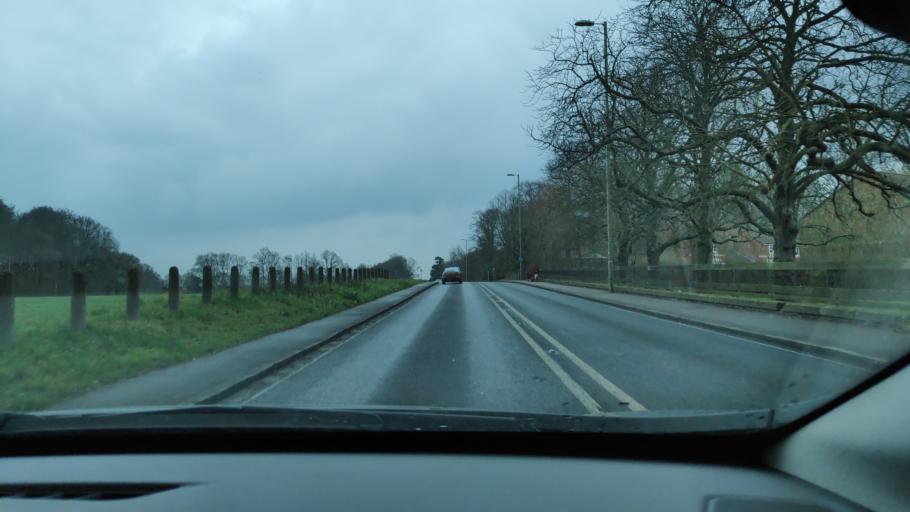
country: GB
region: England
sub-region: Hampshire
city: Aldershot
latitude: 51.2531
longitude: -0.7754
